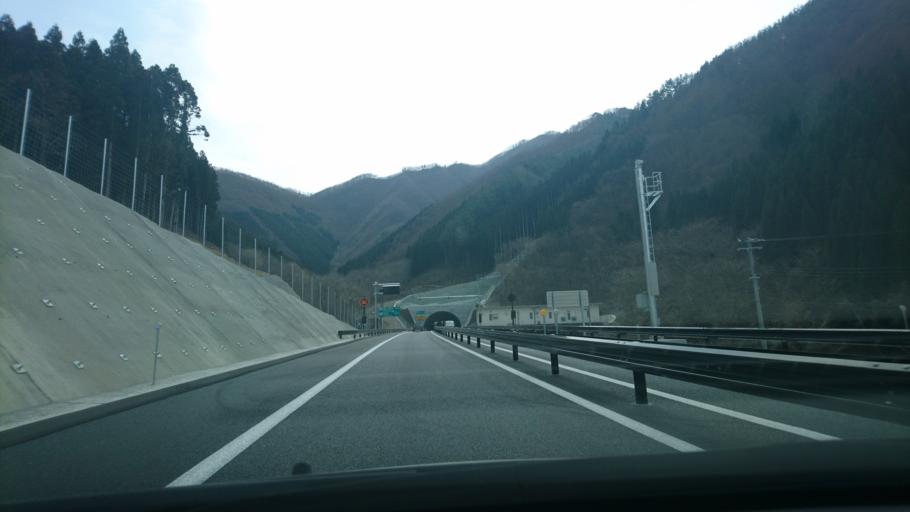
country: JP
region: Iwate
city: Kamaishi
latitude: 39.2443
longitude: 141.8442
